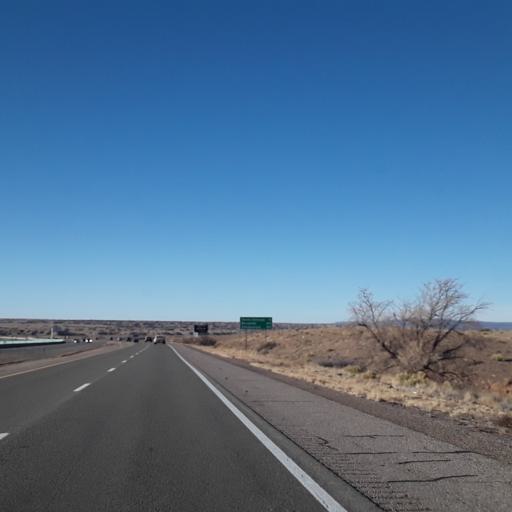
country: US
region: New Mexico
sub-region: Santa Fe County
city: La Cienega
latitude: 35.5098
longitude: -106.2391
